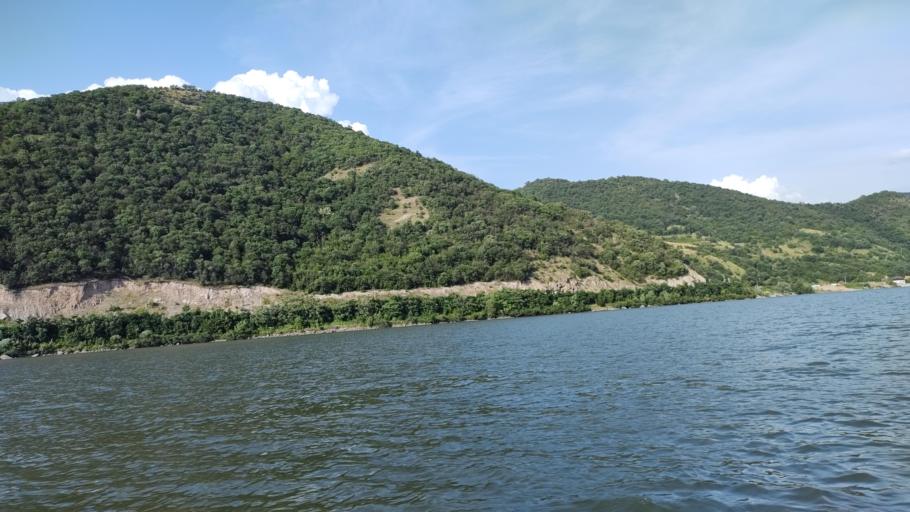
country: RO
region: Mehedinti
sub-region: Comuna Svinita
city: Svinita
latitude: 44.5425
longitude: 22.0482
